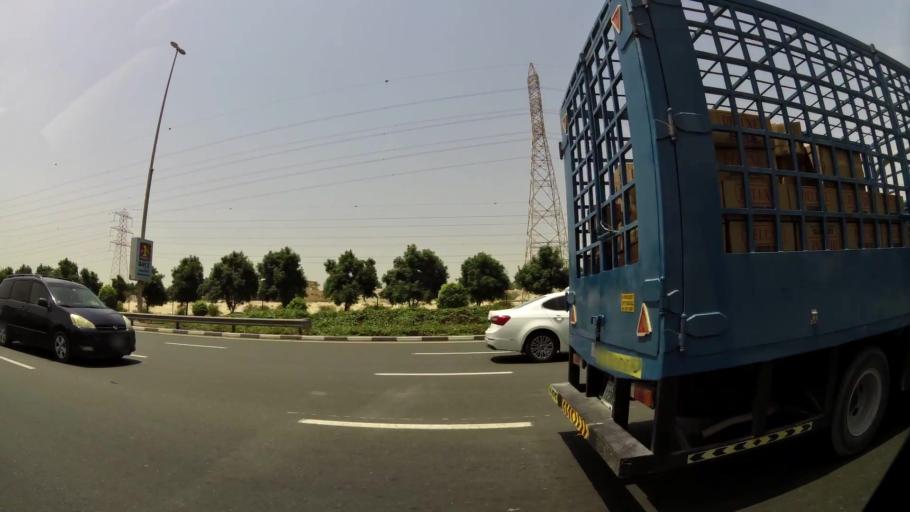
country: AE
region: Ash Shariqah
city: Sharjah
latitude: 25.2126
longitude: 55.3912
